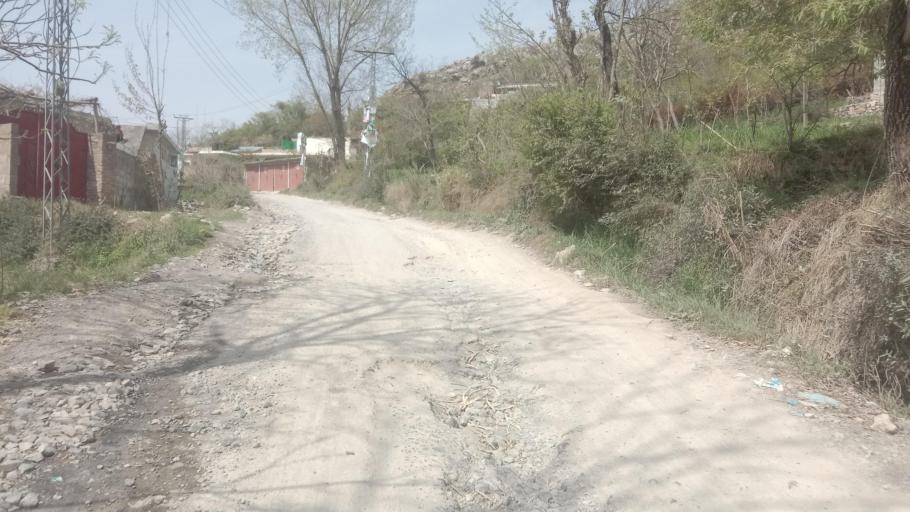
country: PK
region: Khyber Pakhtunkhwa
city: Abbottabad
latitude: 34.1670
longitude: 73.2818
